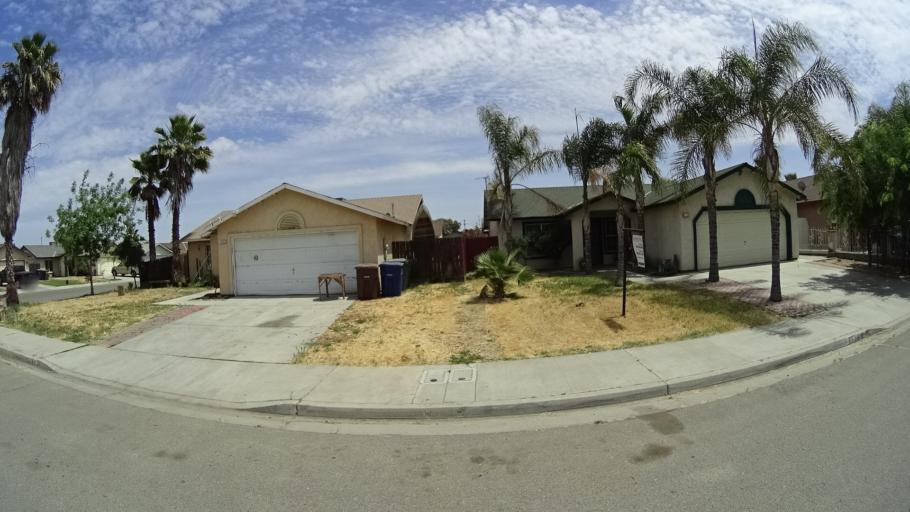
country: US
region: California
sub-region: Kings County
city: Armona
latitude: 36.3114
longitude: -119.7048
